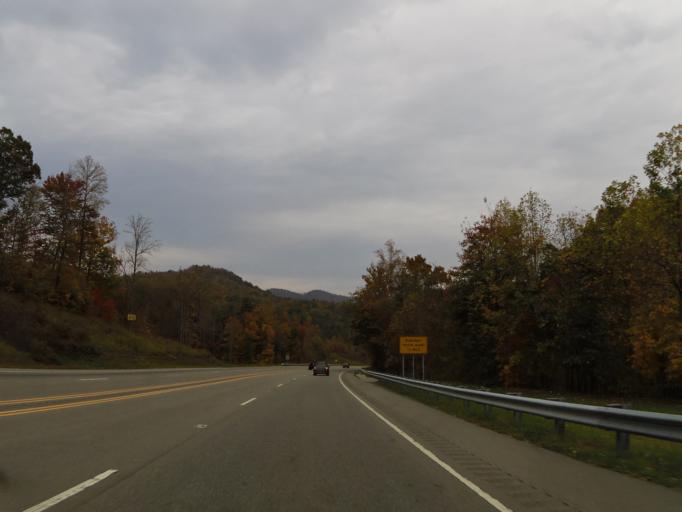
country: US
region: North Carolina
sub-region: Watauga County
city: Blowing Rock
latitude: 36.0566
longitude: -81.5987
